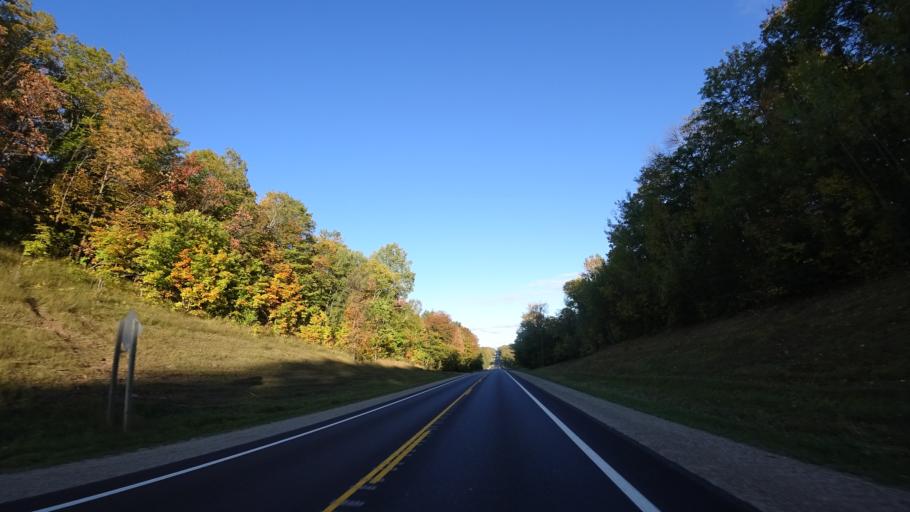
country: US
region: Michigan
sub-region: Luce County
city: Newberry
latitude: 46.3356
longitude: -85.8037
